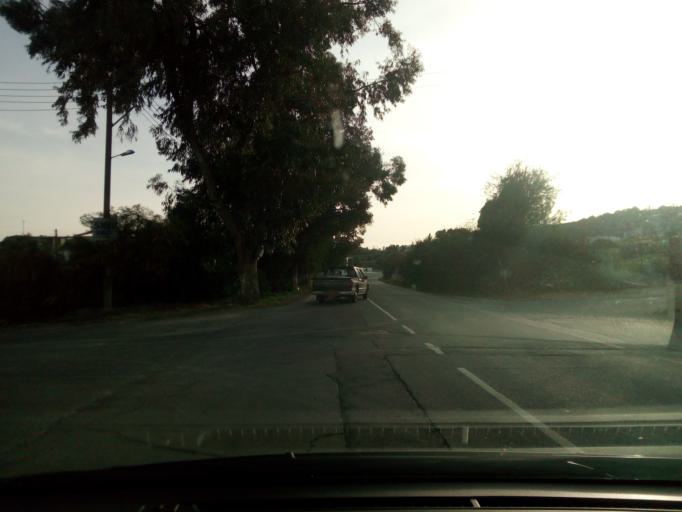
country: CY
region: Larnaka
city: Agios Tychon
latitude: 34.7186
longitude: 33.1331
